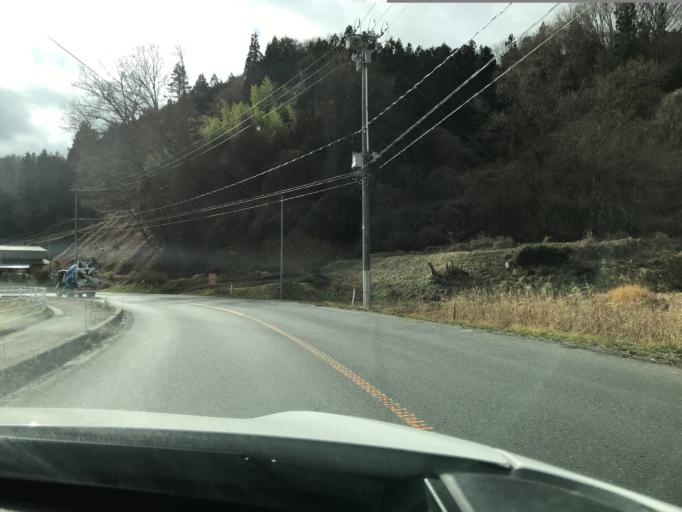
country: JP
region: Fukushima
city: Funehikimachi-funehiki
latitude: 37.5789
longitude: 140.5773
